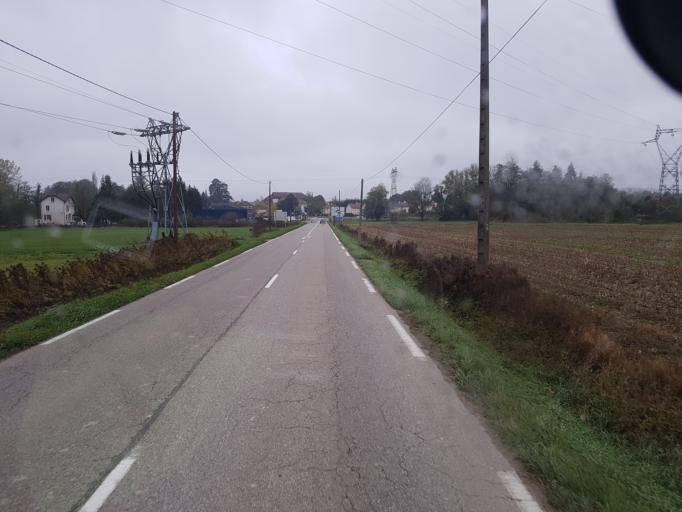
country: FR
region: Rhone-Alpes
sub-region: Departement de l'Isere
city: Aoste
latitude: 45.5819
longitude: 5.6063
